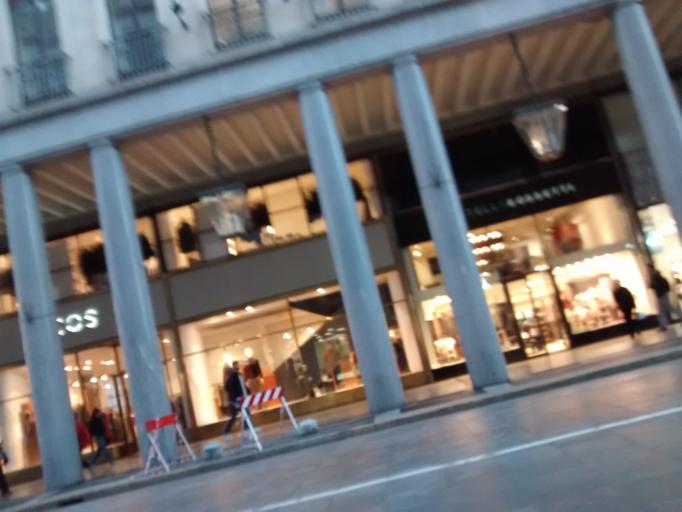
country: IT
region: Piedmont
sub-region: Provincia di Torino
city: Turin
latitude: 45.0651
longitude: 7.6807
